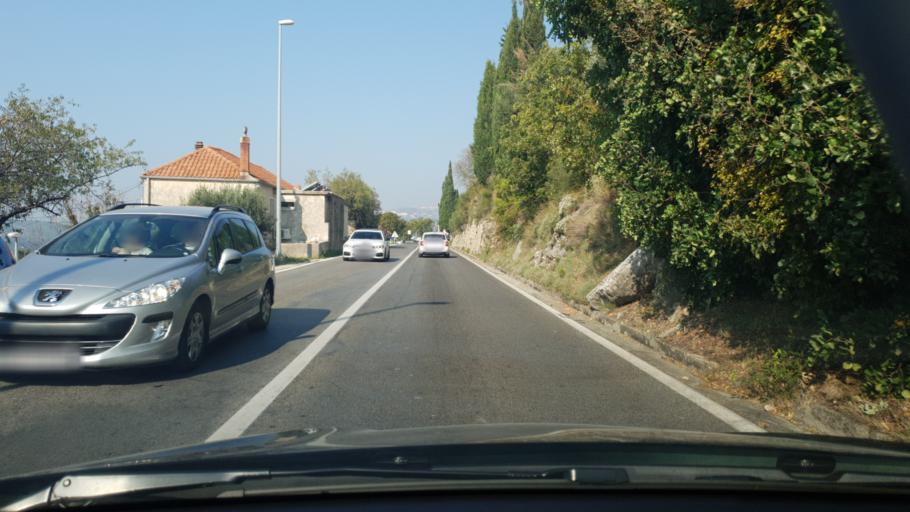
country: HR
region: Dubrovacko-Neretvanska
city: Cavtat
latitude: 42.6159
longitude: 18.2176
